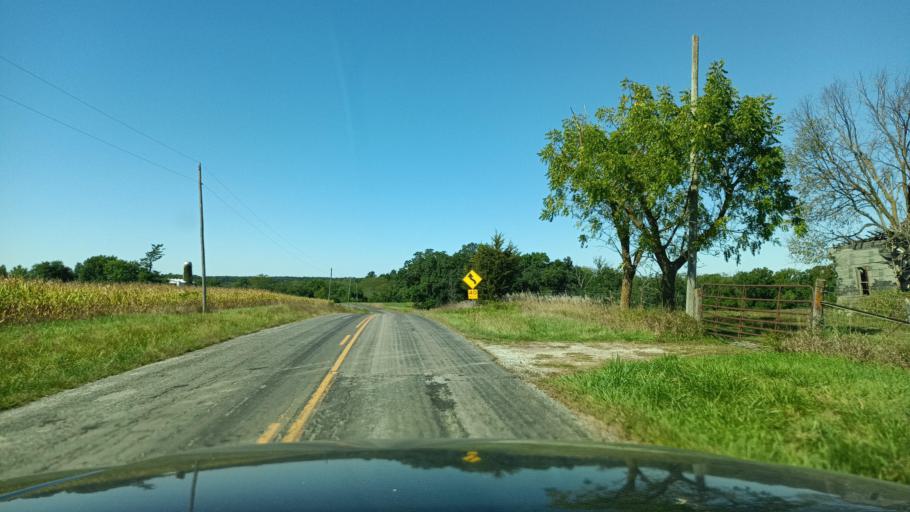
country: US
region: Missouri
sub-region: Scotland County
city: Memphis
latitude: 40.3547
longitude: -92.2328
